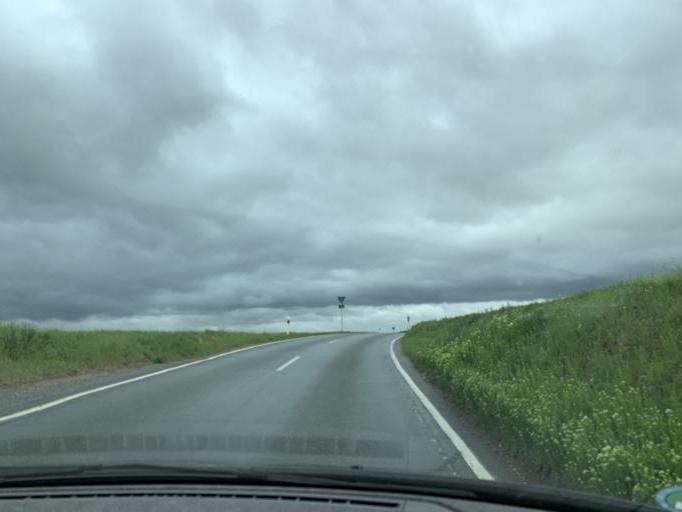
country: DE
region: North Rhine-Westphalia
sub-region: Regierungsbezirk Koln
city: Mechernich
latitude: 50.6301
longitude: 6.7048
